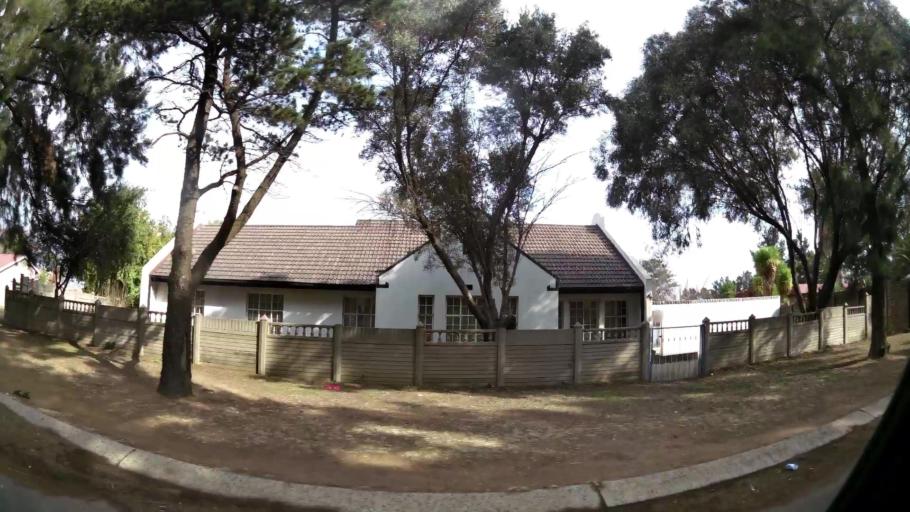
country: ZA
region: Gauteng
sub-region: Sedibeng District Municipality
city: Vanderbijlpark
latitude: -26.7070
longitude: 27.8033
